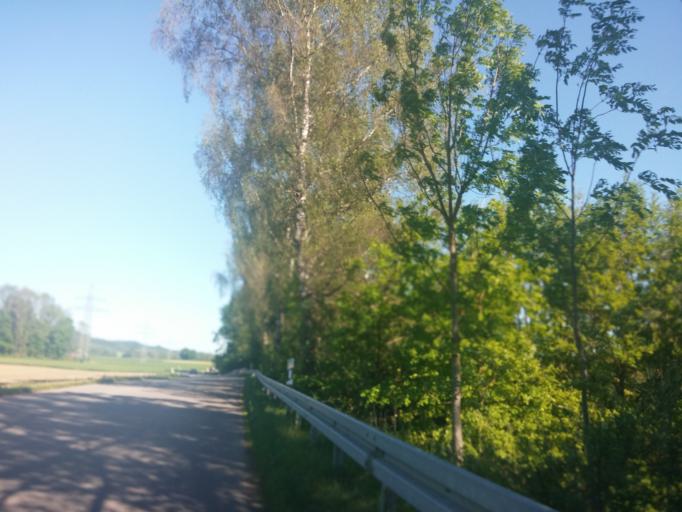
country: DE
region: Bavaria
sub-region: Swabia
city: Lautrach
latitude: 47.8993
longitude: 10.1364
